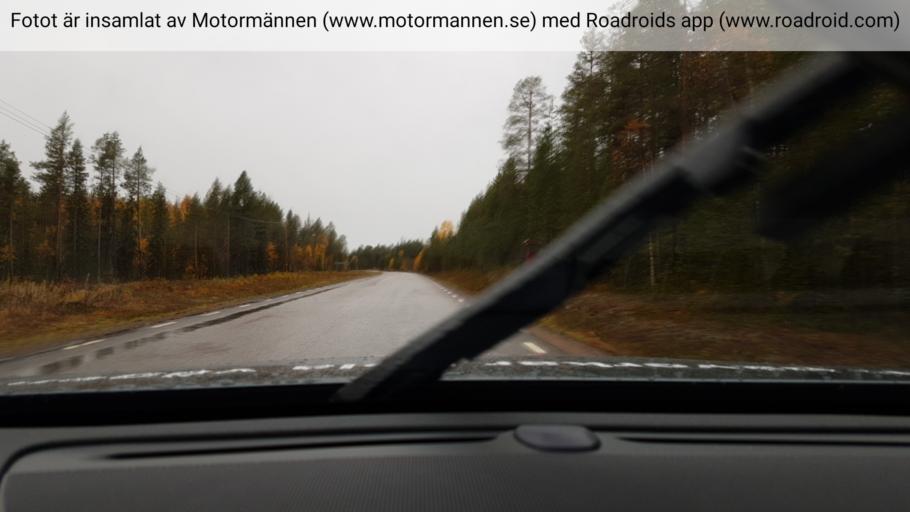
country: SE
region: Norrbotten
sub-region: Pajala Kommun
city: Pajala
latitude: 66.9318
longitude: 22.9918
